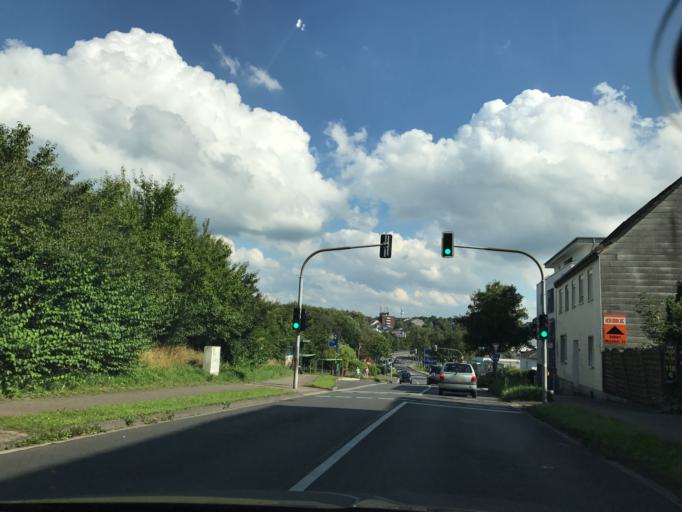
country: DE
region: North Rhine-Westphalia
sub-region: Regierungsbezirk Dusseldorf
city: Velbert
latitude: 51.3508
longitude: 7.0234
